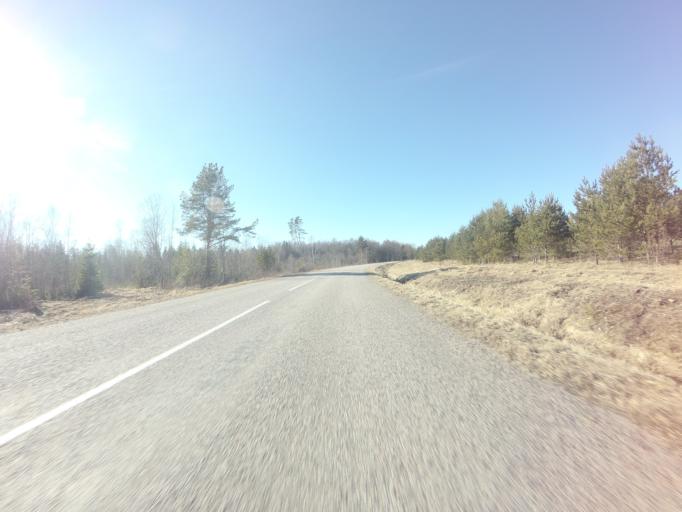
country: EE
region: Saare
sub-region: Kuressaare linn
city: Kuressaare
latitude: 58.5671
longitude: 22.4743
